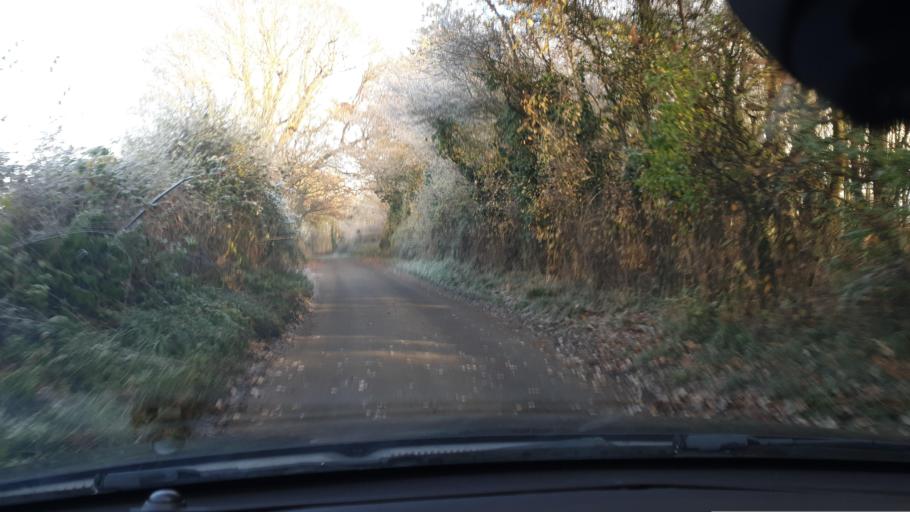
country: GB
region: England
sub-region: Essex
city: Mistley
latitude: 51.9811
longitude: 1.1129
